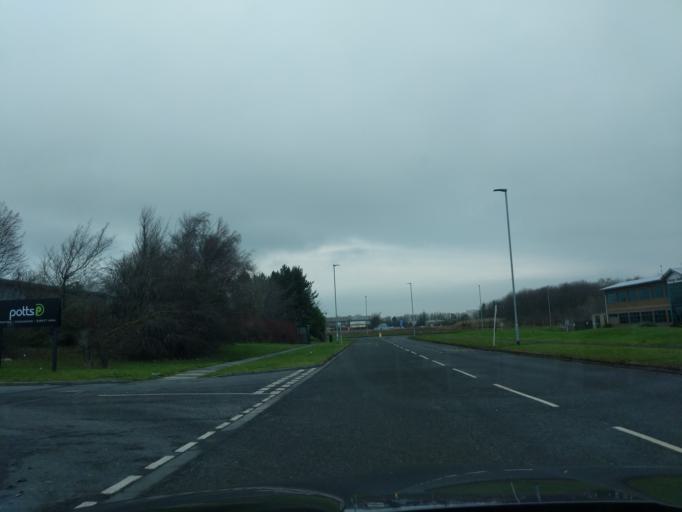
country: GB
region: England
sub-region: Northumberland
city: Cramlington
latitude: 55.0994
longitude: -1.6100
